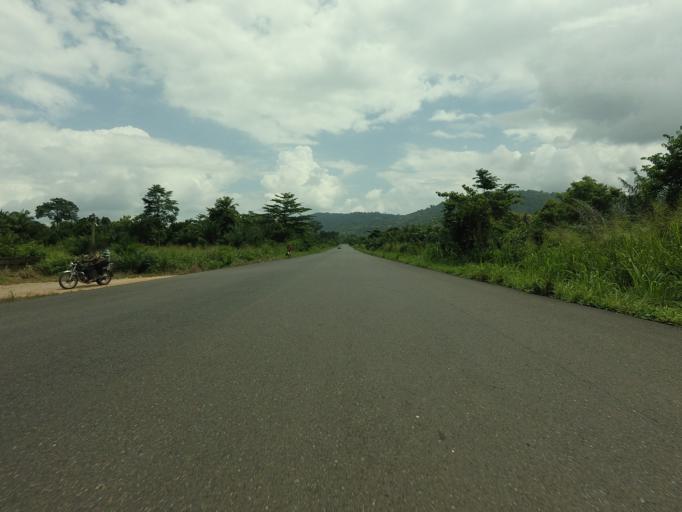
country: GH
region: Volta
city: Ho
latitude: 6.5410
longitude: 0.2420
